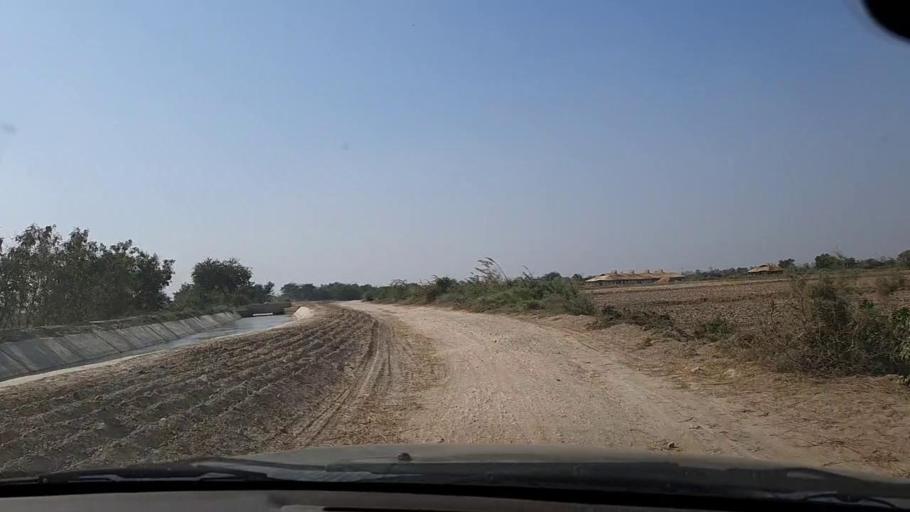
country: PK
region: Sindh
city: Chuhar Jamali
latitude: 24.4282
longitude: 67.8026
